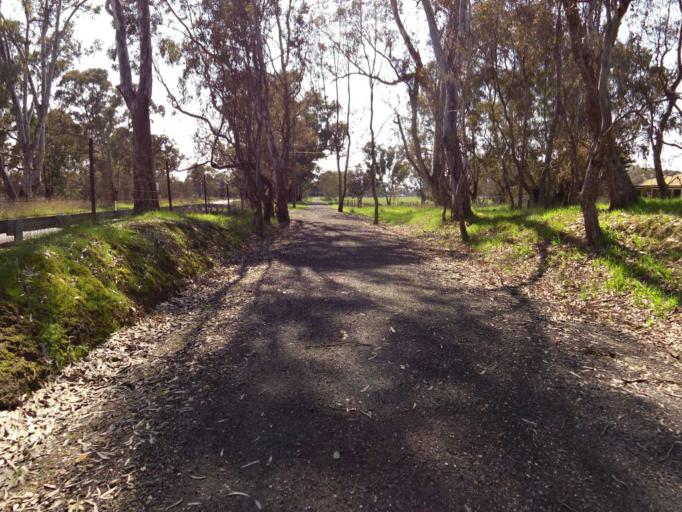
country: AU
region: Victoria
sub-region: Murrindindi
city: Alexandra
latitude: -37.1160
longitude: 145.6061
